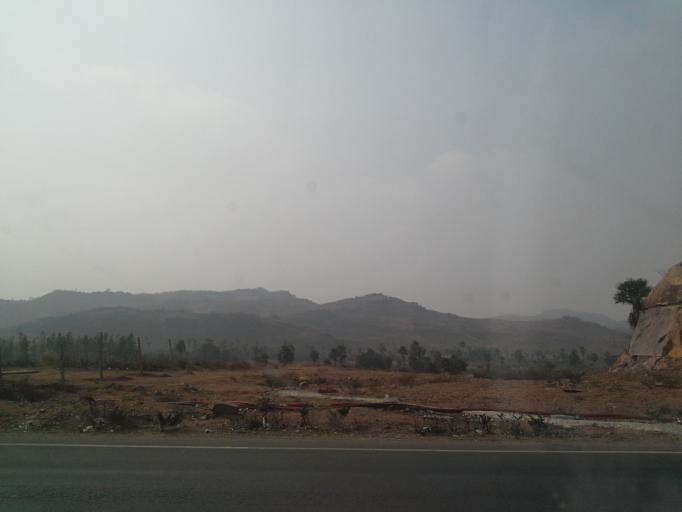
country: IN
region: Telangana
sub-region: Rangareddi
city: Lal Bahadur Nagar
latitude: 17.3152
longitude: 78.6734
